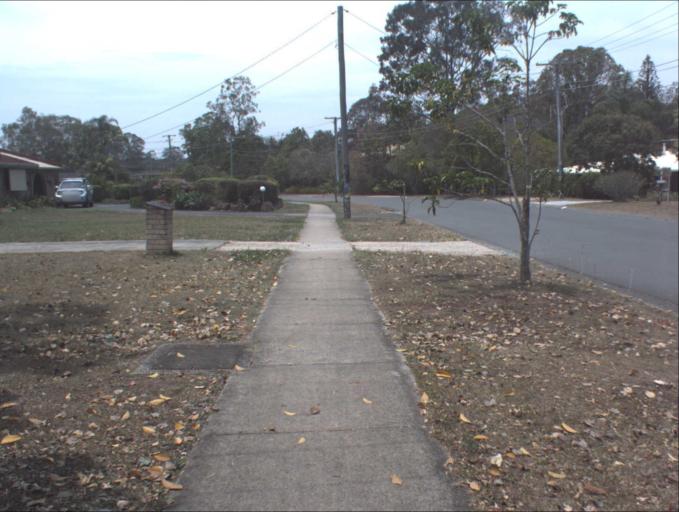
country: AU
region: Queensland
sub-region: Logan
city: Slacks Creek
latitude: -27.6704
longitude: 153.1835
